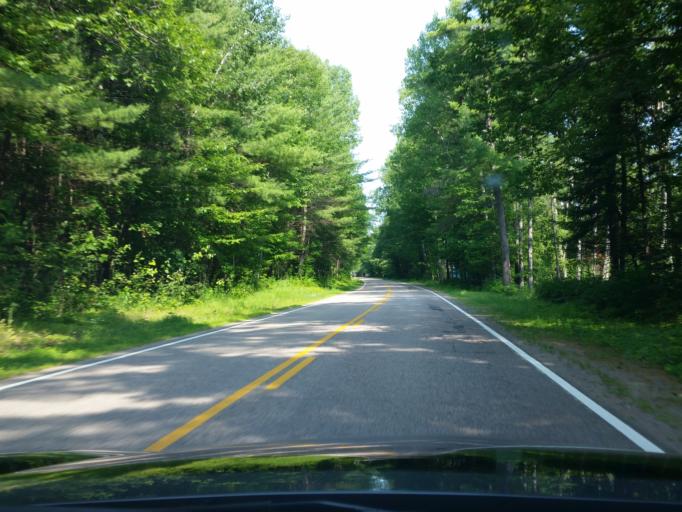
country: CA
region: Quebec
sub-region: Outaouais
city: Shawville
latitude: 45.5221
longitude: -76.4339
